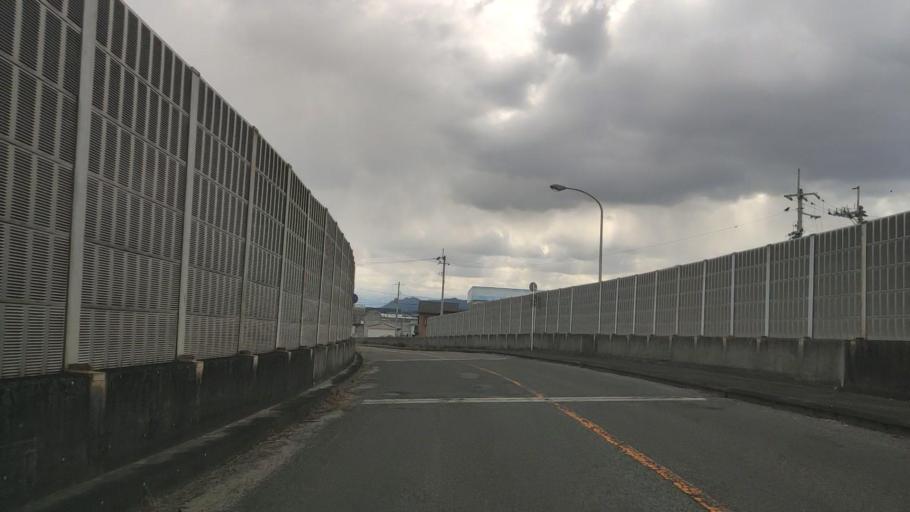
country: JP
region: Ehime
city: Saijo
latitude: 34.0586
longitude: 133.0175
